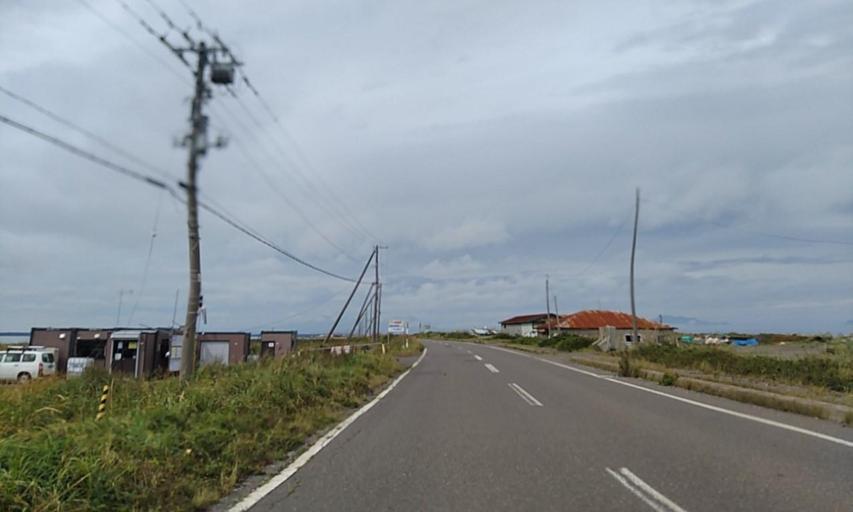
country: JP
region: Hokkaido
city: Shibetsu
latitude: 43.6097
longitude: 145.2710
